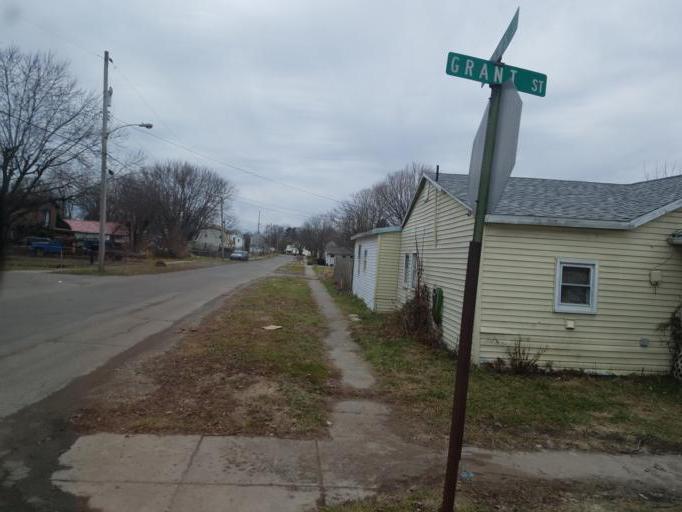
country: US
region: Ohio
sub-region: Marion County
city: Marion
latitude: 40.5962
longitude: -83.1180
